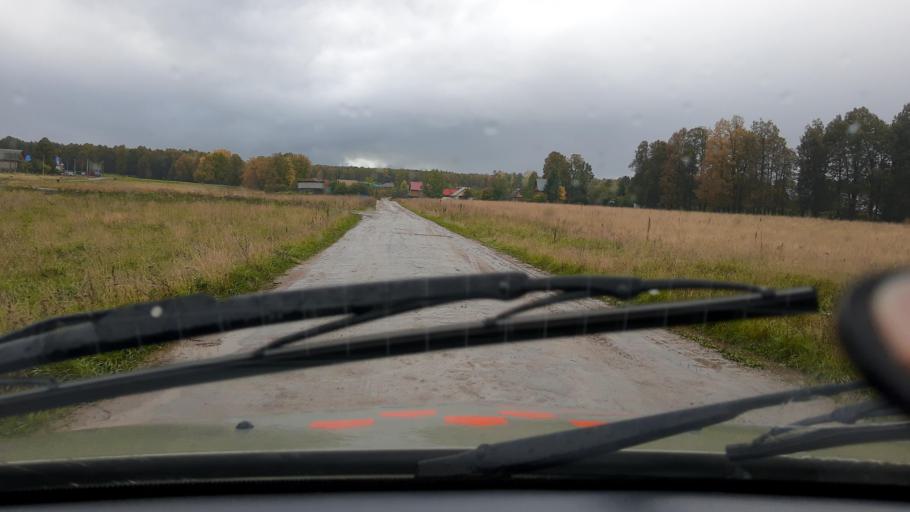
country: RU
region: Bashkortostan
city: Kudeyevskiy
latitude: 54.8777
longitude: 56.6293
